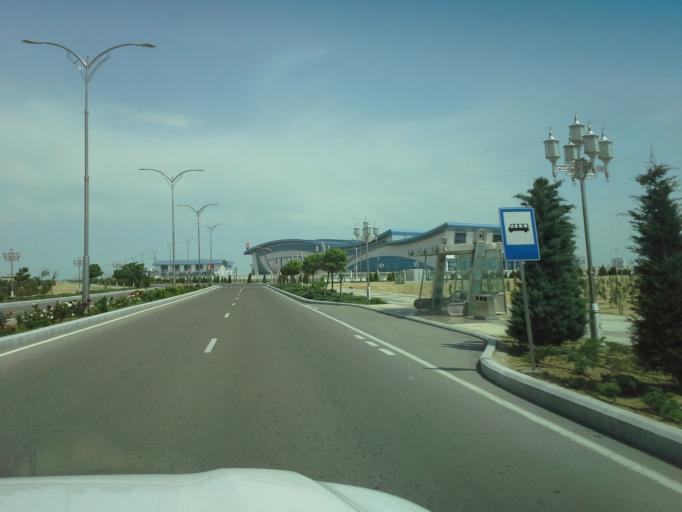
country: TM
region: Balkan
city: Turkmenbasy
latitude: 39.9670
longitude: 52.8479
